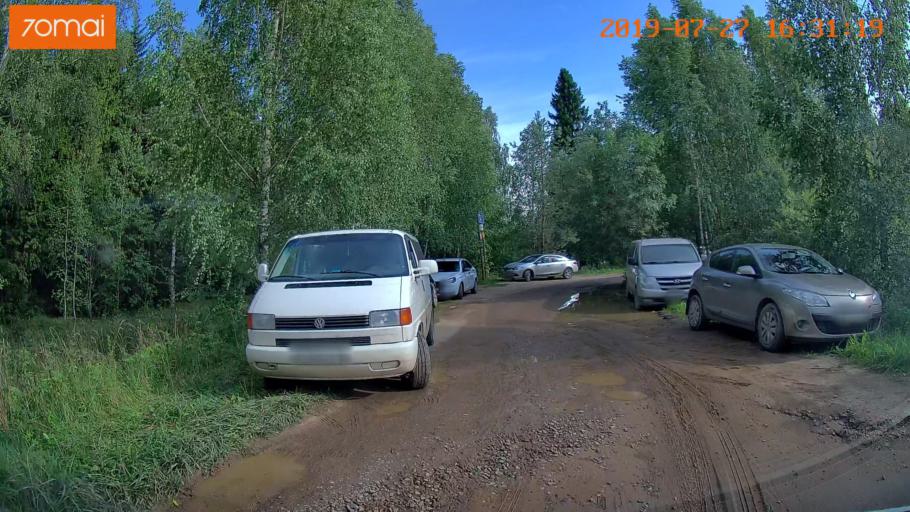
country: RU
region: Ivanovo
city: Novo-Talitsy
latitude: 57.0910
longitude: 40.8529
